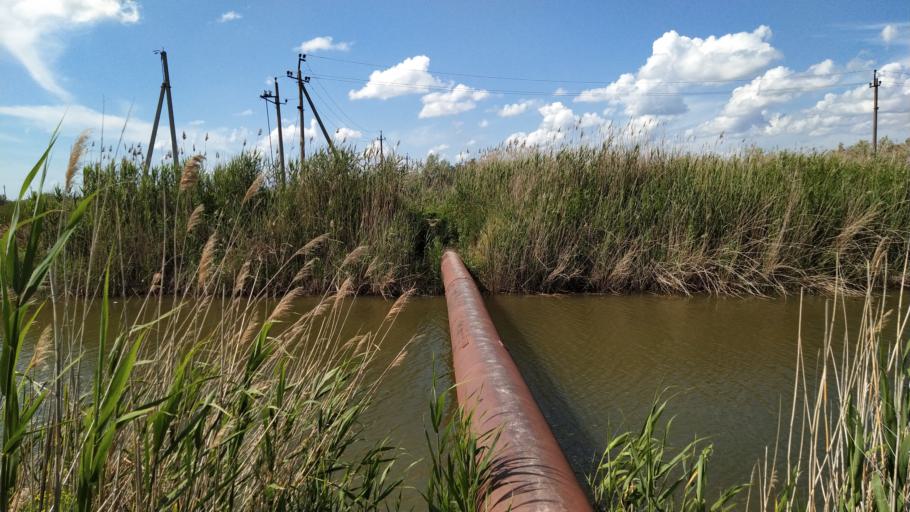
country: RU
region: Rostov
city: Bataysk
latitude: 47.1409
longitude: 39.6689
